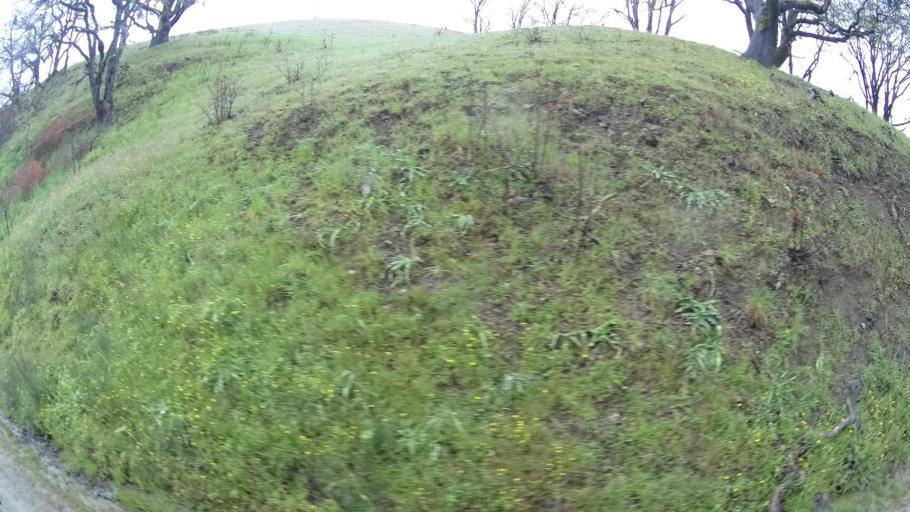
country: US
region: California
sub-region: Humboldt County
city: Westhaven-Moonstone
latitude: 41.1468
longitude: -123.8895
